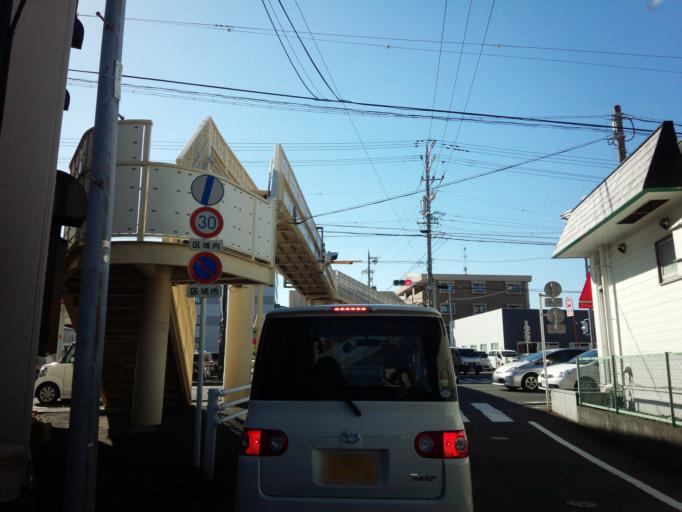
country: JP
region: Shizuoka
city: Shizuoka-shi
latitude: 34.9557
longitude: 138.3824
